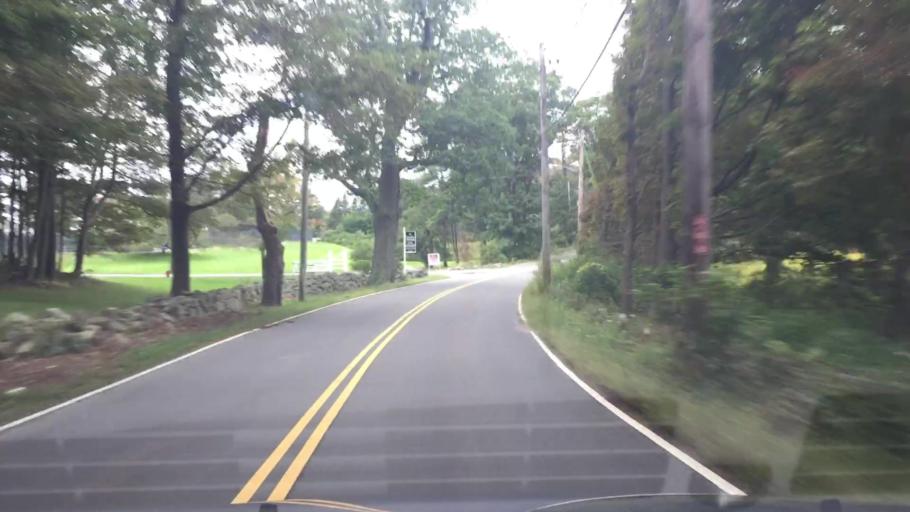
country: US
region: Massachusetts
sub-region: Essex County
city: North Andover
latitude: 42.7052
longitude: -71.0809
